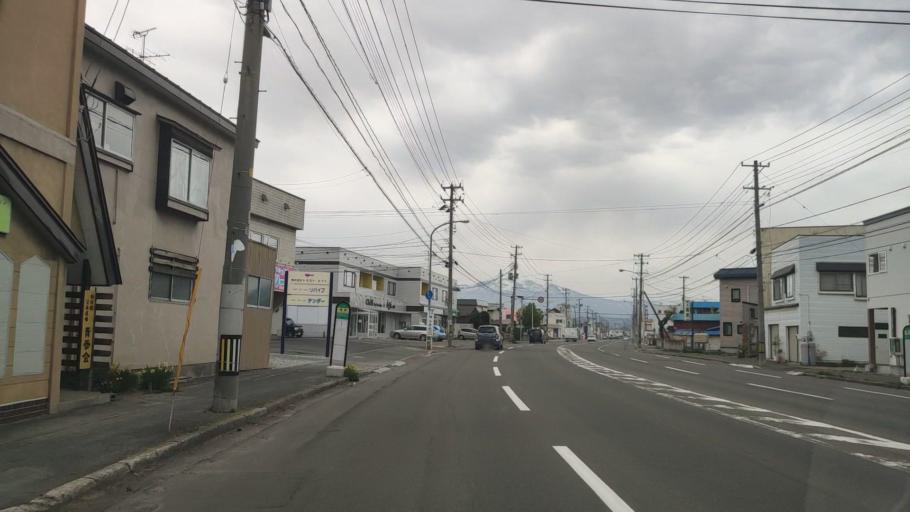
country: JP
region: Aomori
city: Aomori Shi
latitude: 40.8181
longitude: 140.7743
